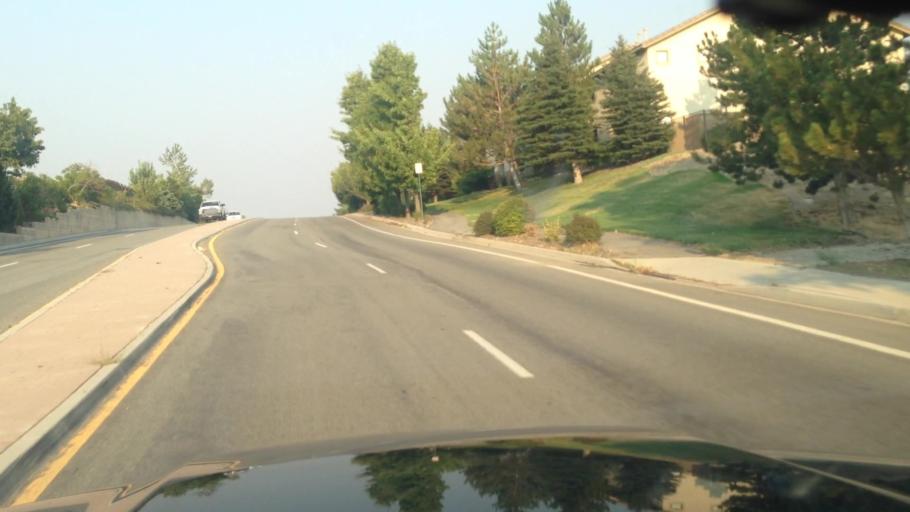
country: US
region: Nevada
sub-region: Washoe County
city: Mogul
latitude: 39.5190
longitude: -119.8932
